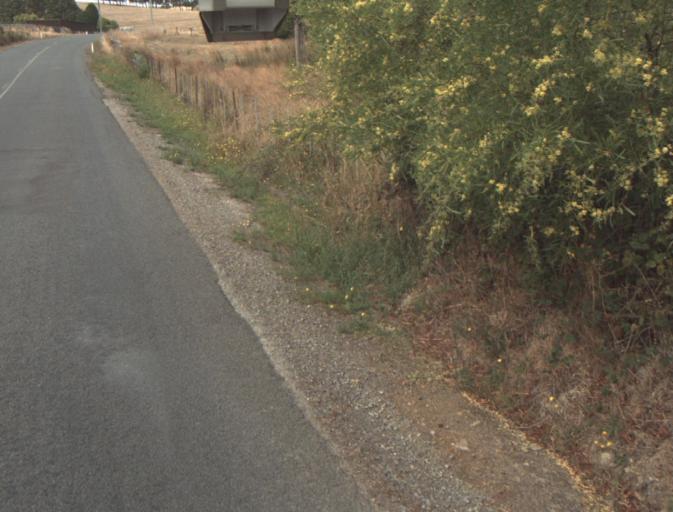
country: AU
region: Tasmania
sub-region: Launceston
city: Mayfield
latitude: -41.1930
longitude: 147.2208
